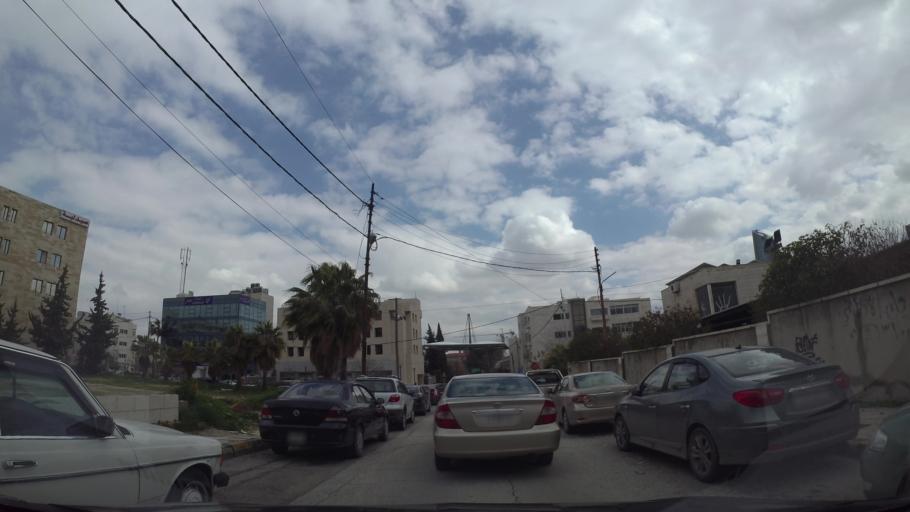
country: JO
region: Amman
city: Amman
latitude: 31.9699
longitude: 35.8990
